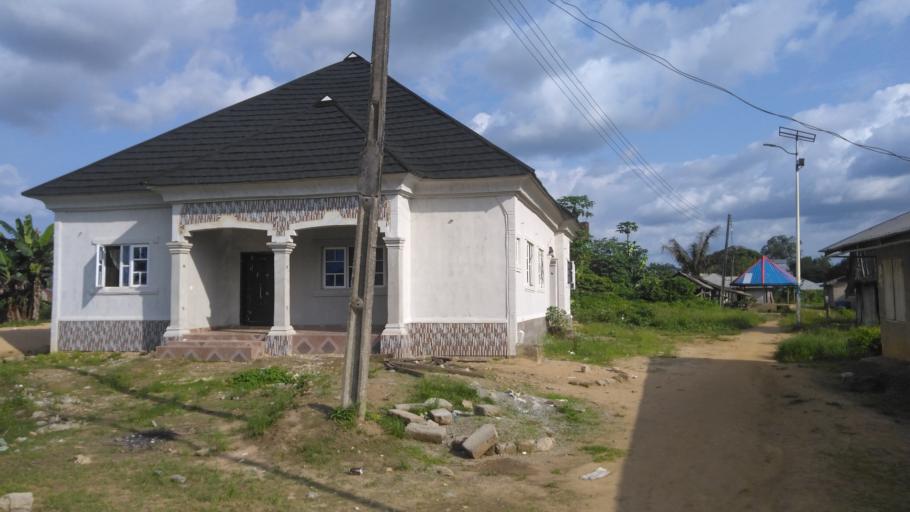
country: NG
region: Edo
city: Siluko
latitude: 6.1440
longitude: 5.2002
